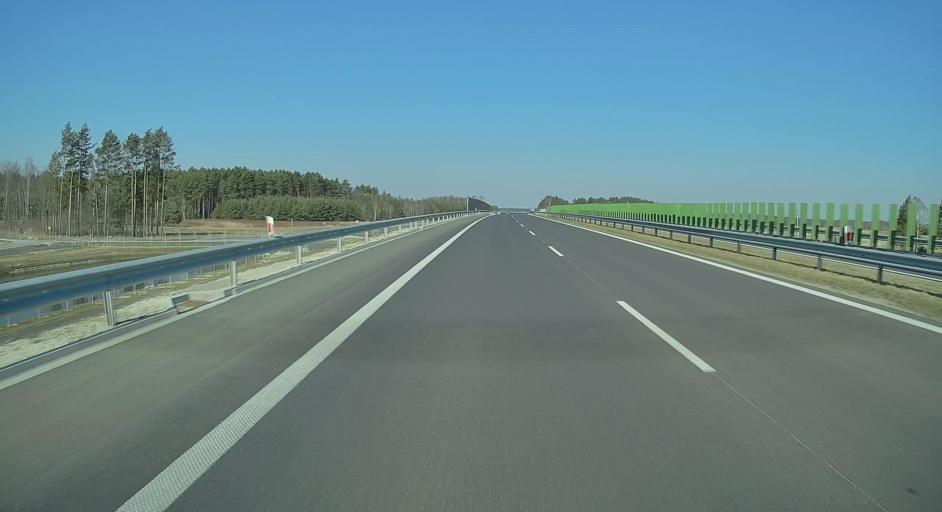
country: PL
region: Subcarpathian Voivodeship
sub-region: Powiat nizanski
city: Konczyce
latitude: 50.4025
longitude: 22.1374
